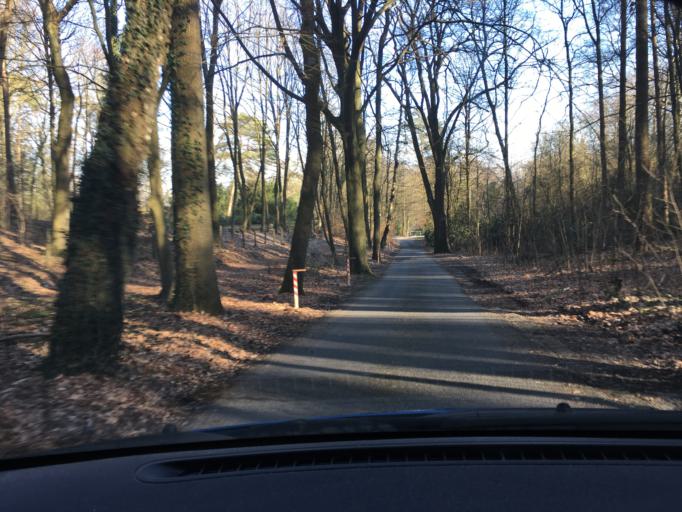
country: DE
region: Lower Saxony
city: Seevetal
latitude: 53.3942
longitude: 9.9533
